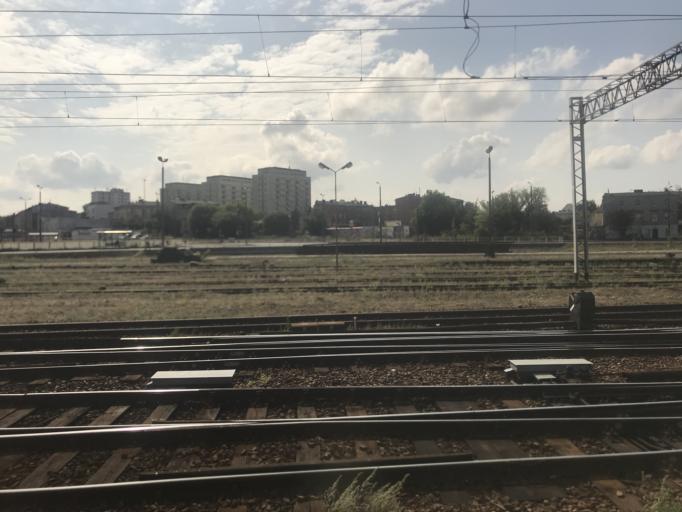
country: PL
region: Kujawsko-Pomorskie
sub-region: Bydgoszcz
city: Bydgoszcz
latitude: 53.1376
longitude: 17.9977
